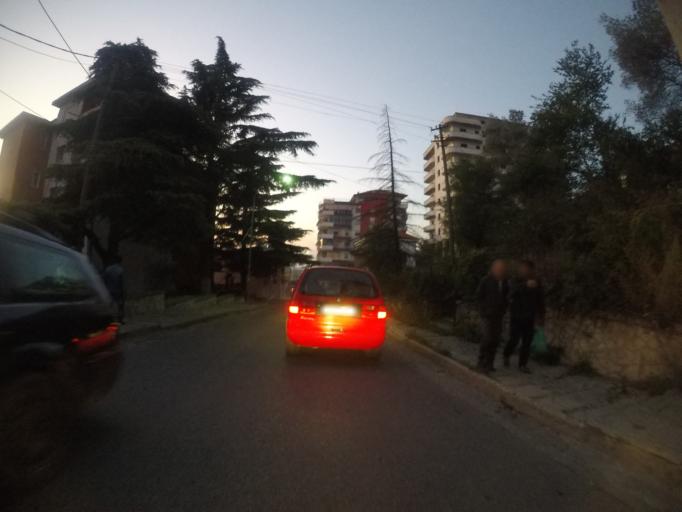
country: AL
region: Durres
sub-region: Rrethi i Krujes
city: Kruje
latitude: 41.5135
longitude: 19.7903
